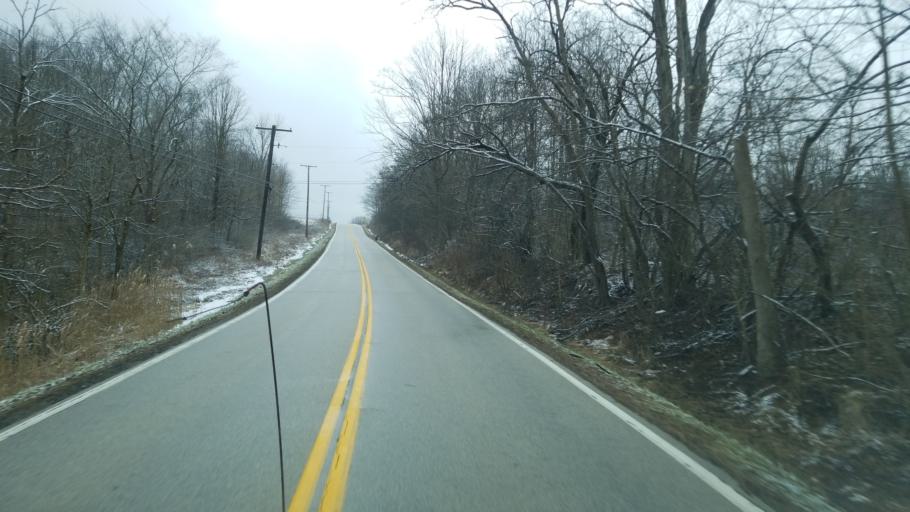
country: US
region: Ohio
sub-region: Portage County
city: Aurora
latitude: 41.2908
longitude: -81.3213
